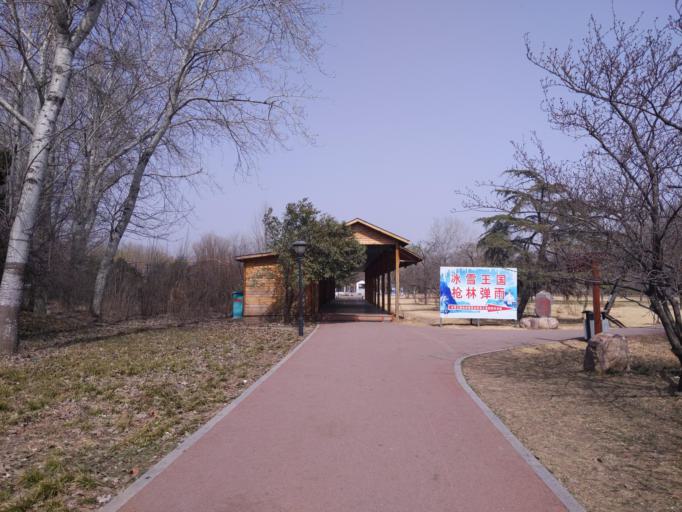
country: CN
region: Henan Sheng
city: Puyang
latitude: 35.7760
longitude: 114.9626
